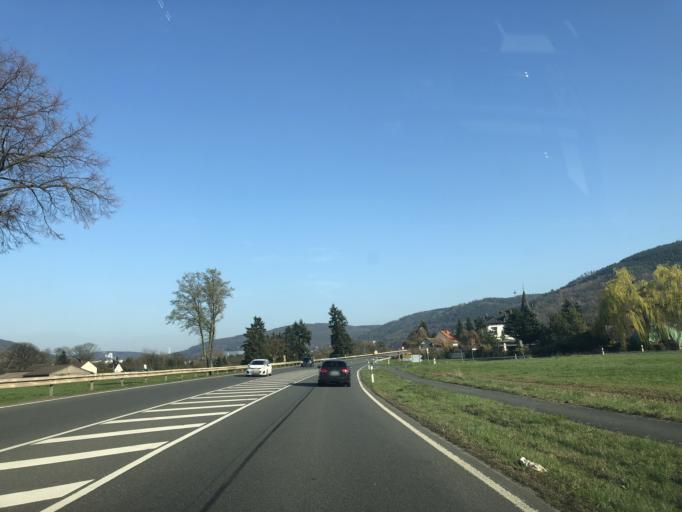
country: DE
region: Bavaria
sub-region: Regierungsbezirk Unterfranken
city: Kleinheubach
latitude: 49.7097
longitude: 9.2246
